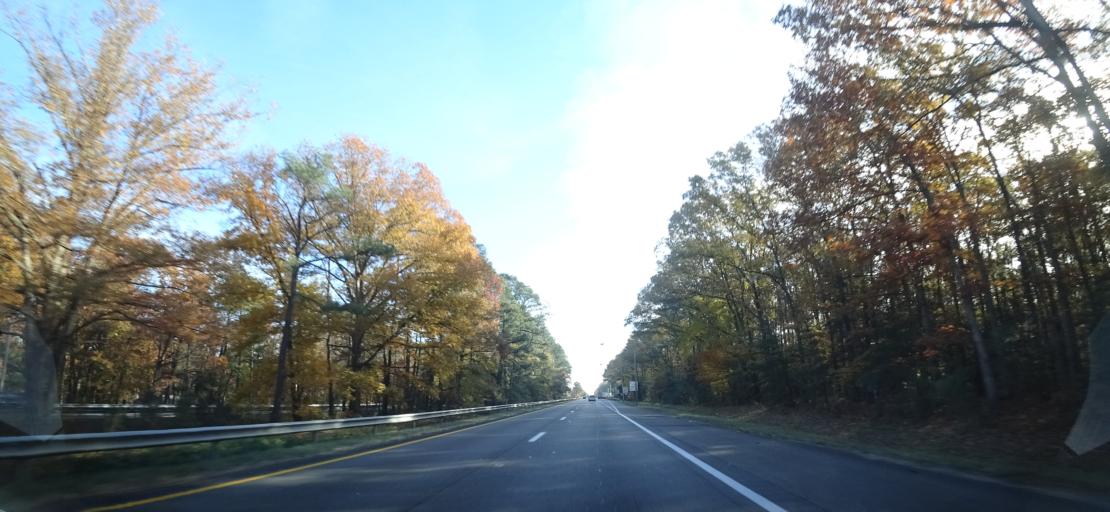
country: US
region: Virginia
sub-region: Henrico County
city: Sandston
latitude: 37.5138
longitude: -77.2380
